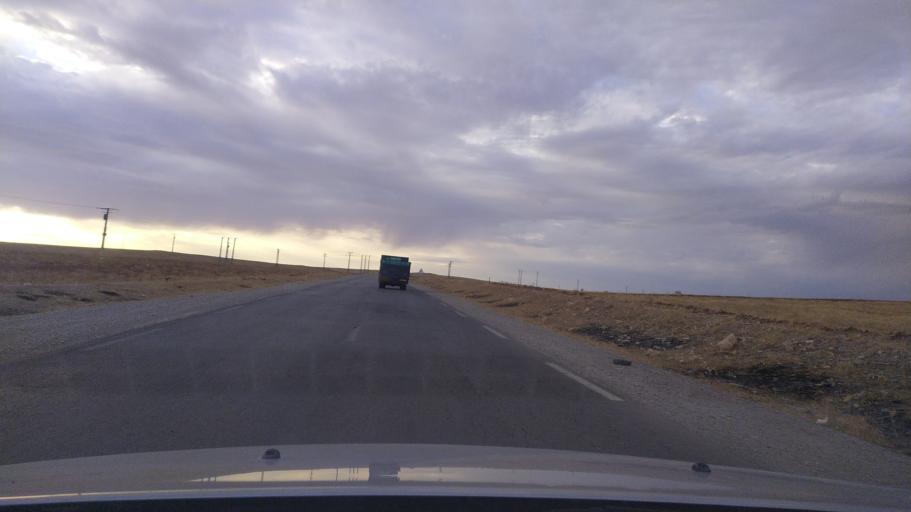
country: DZ
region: Tiaret
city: Frenda
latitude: 34.9870
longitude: 1.1350
